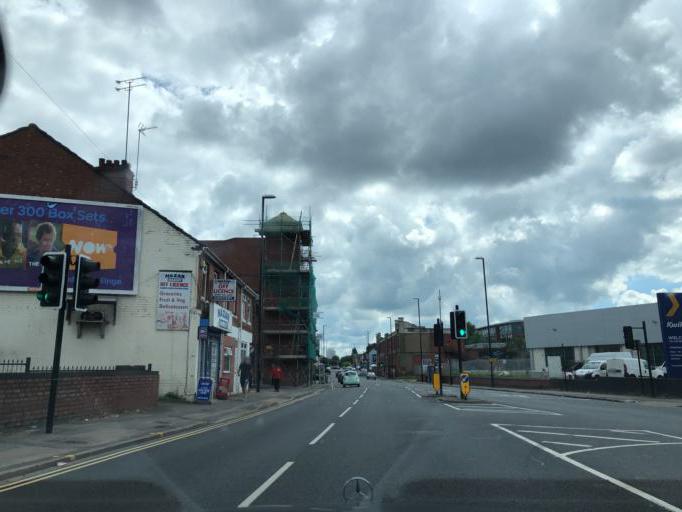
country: GB
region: England
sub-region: Coventry
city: Coventry
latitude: 52.4215
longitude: -1.5054
